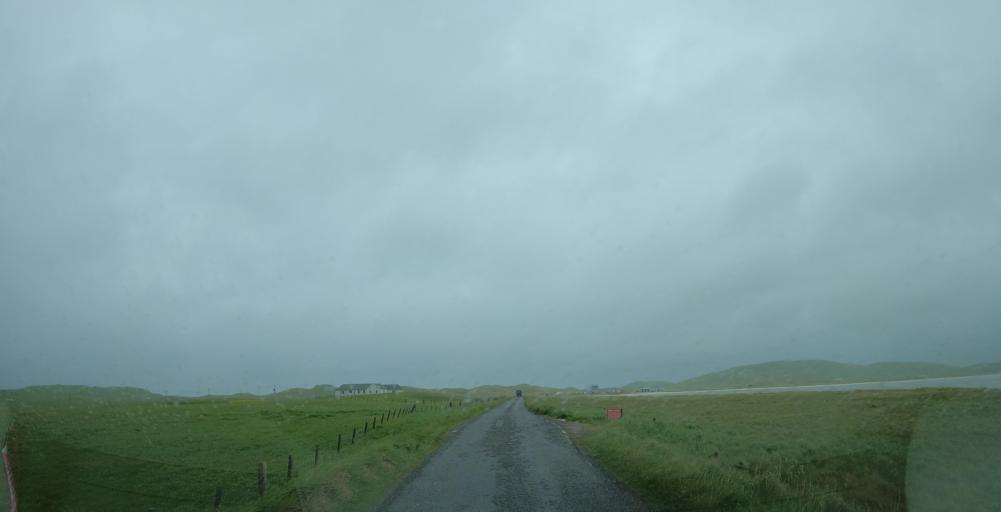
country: GB
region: Scotland
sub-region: Eilean Siar
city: Barra
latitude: 57.0212
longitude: -7.4479
